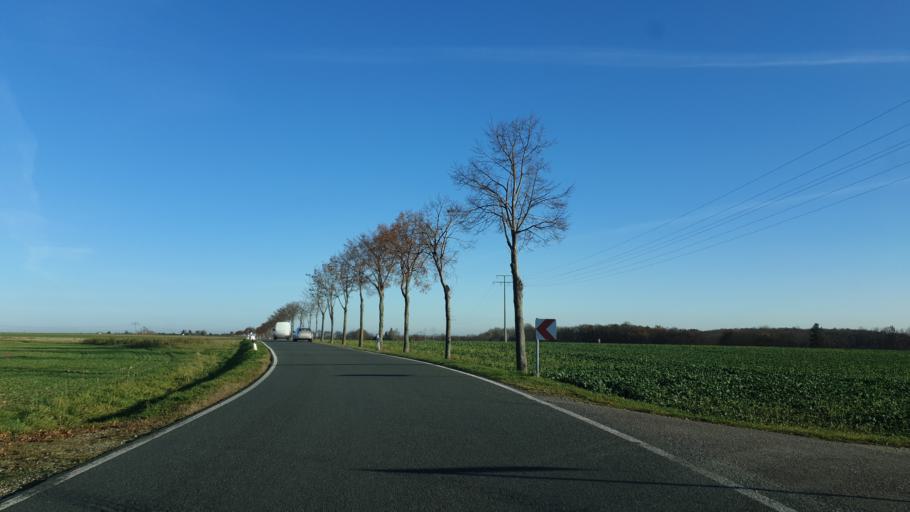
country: DE
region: Thuringia
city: Eisenberg
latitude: 50.9709
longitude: 11.9185
